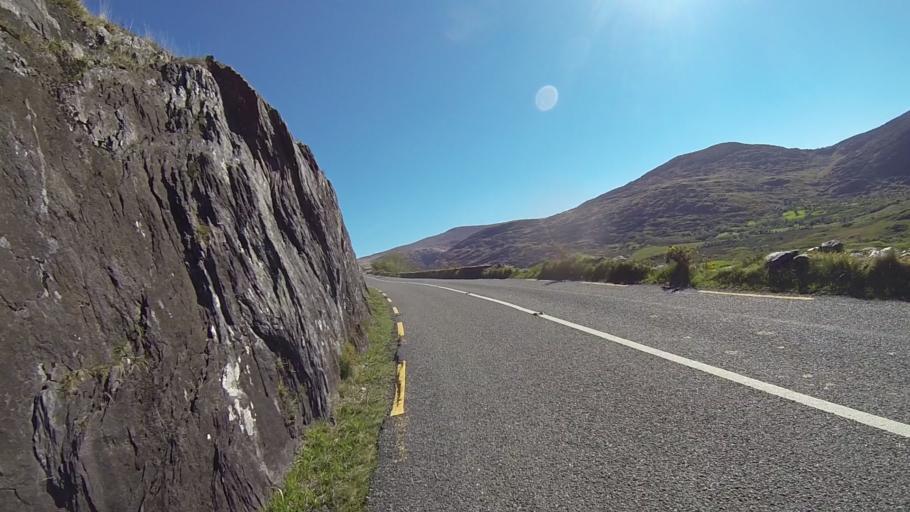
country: IE
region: Munster
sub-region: Ciarrai
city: Kenmare
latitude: 51.7723
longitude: -9.7399
